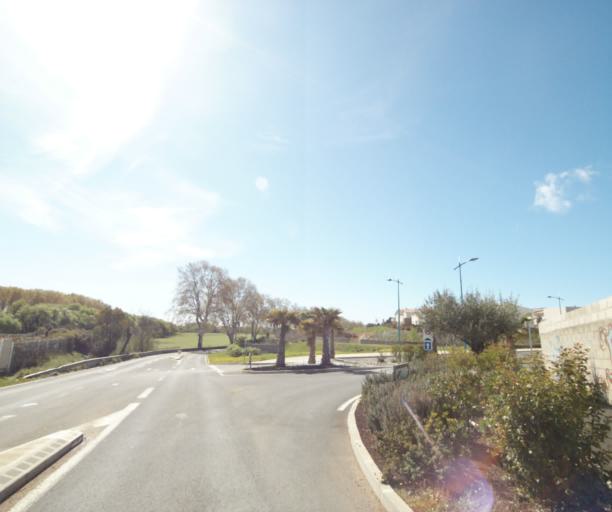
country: FR
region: Languedoc-Roussillon
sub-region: Departement de l'Herault
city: Villeneuve-les-Maguelone
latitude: 43.5535
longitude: 3.8457
